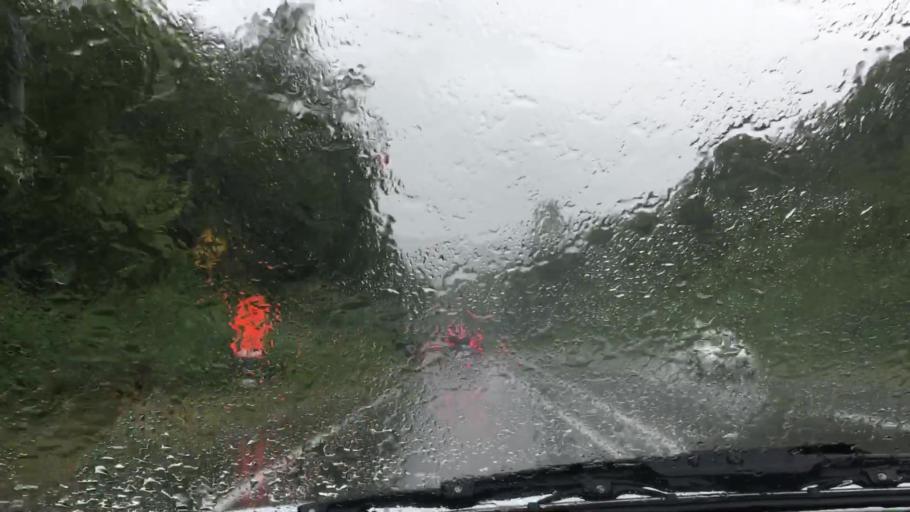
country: JP
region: Hokkaido
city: Sapporo
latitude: 42.8501
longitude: 141.0806
